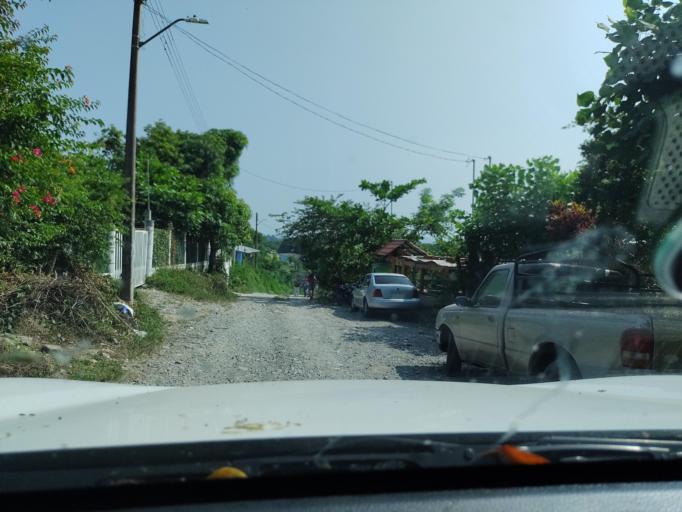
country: MX
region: Veracruz
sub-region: Martinez de la Torre
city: El Progreso
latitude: 20.0794
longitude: -97.0029
